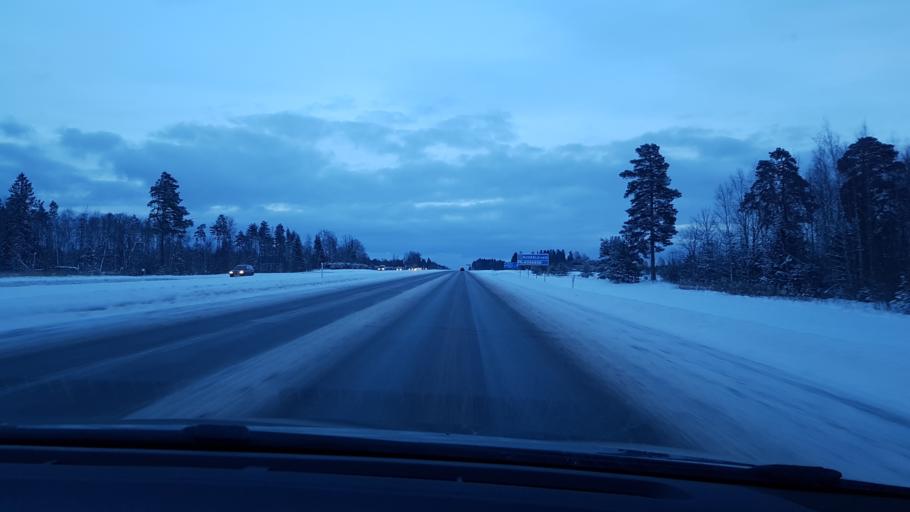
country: EE
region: Harju
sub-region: Raasiku vald
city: Raasiku
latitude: 59.4388
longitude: 25.2620
